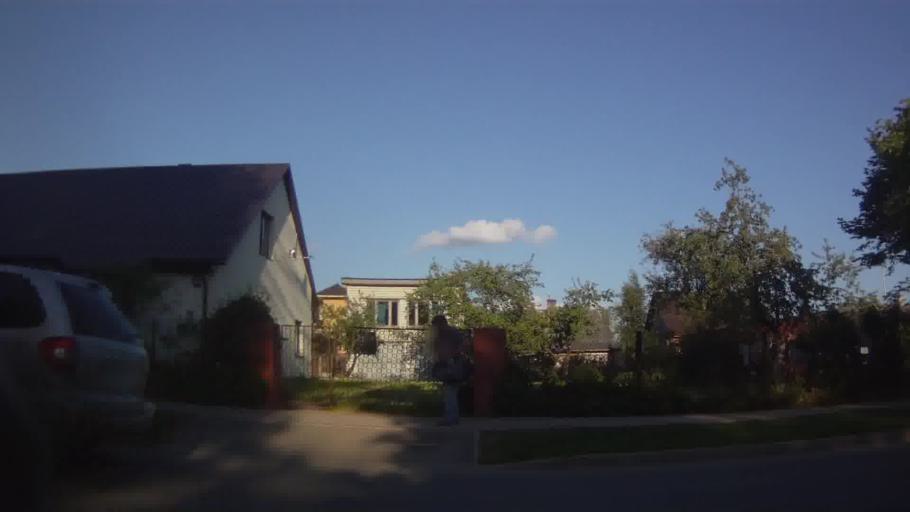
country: LV
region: Rezekne
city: Rezekne
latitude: 56.5117
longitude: 27.3401
